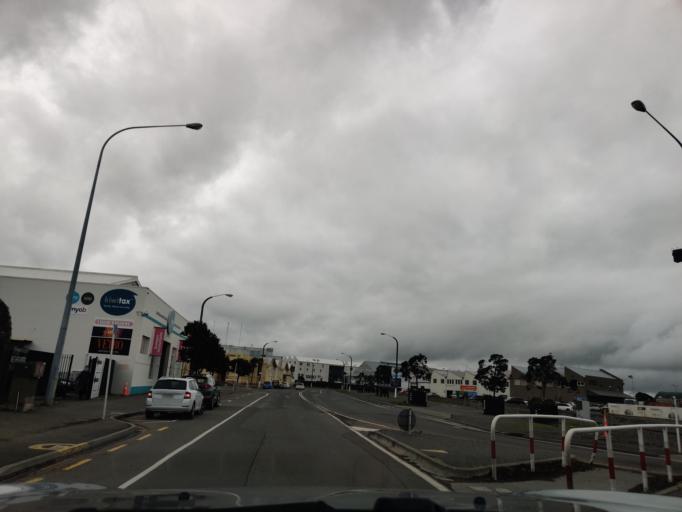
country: NZ
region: Hawke's Bay
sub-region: Napier City
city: Napier
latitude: -39.4823
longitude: 176.8968
